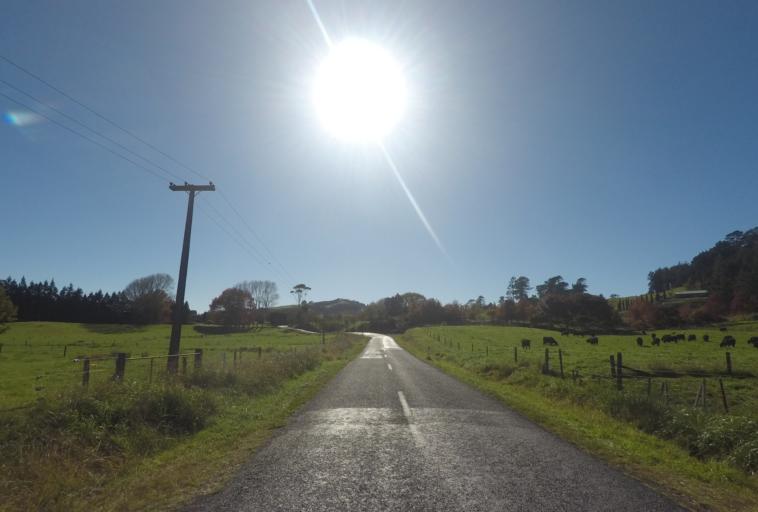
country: NZ
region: Bay of Plenty
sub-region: Western Bay of Plenty District
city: Waihi Beach
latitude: -37.4052
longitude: 175.9045
